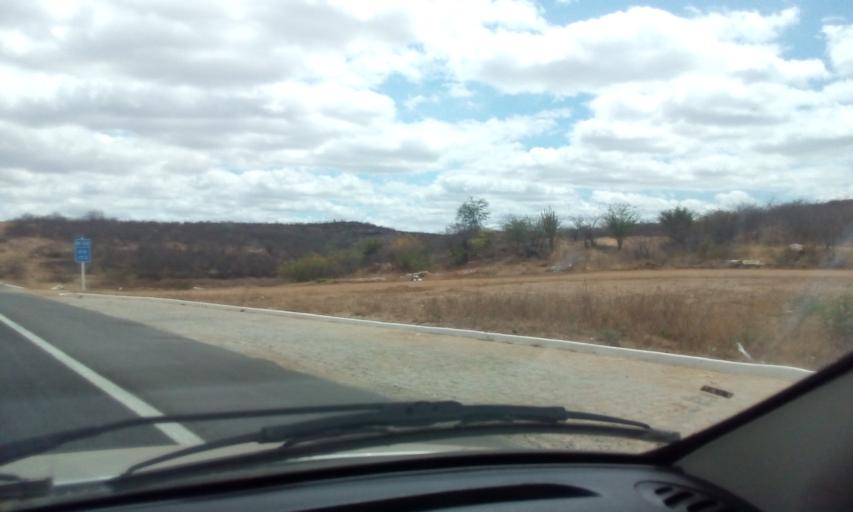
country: BR
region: Rio Grande do Norte
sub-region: Currais Novos
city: Currais Novos
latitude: -6.2569
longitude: -36.4923
